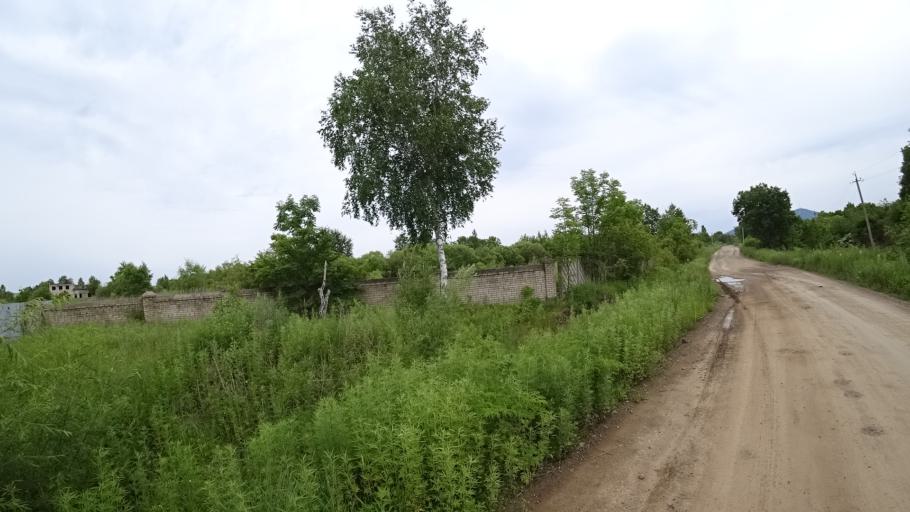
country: RU
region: Primorskiy
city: Arsen'yev
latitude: 44.1969
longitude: 133.3076
